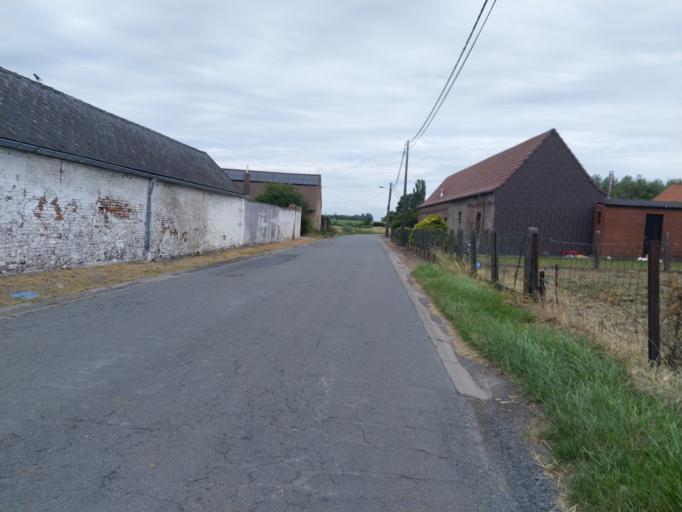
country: BE
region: Wallonia
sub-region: Province du Hainaut
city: Beloeil
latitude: 50.5486
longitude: 3.7515
